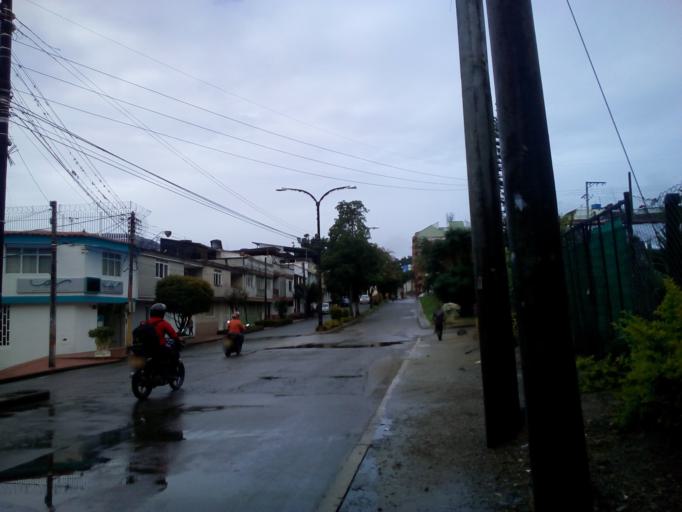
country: CO
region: Tolima
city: Ibague
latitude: 4.4490
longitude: -75.2441
